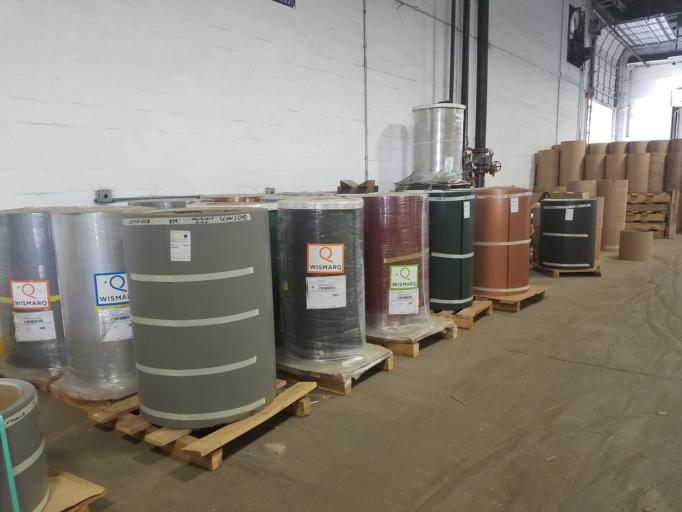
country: US
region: Kentucky
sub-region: Jefferson County
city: Audubon Park
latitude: 38.1929
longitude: -85.7013
